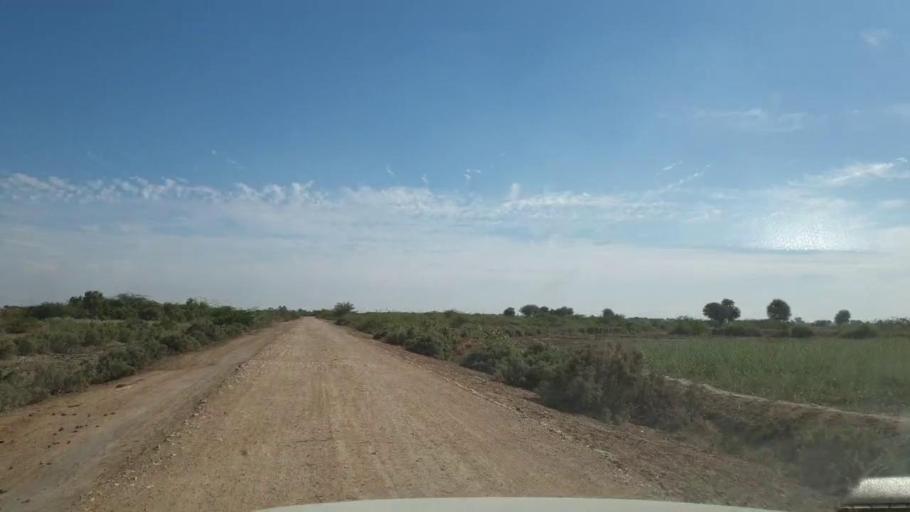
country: PK
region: Sindh
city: Pithoro
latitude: 25.5890
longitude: 69.2857
